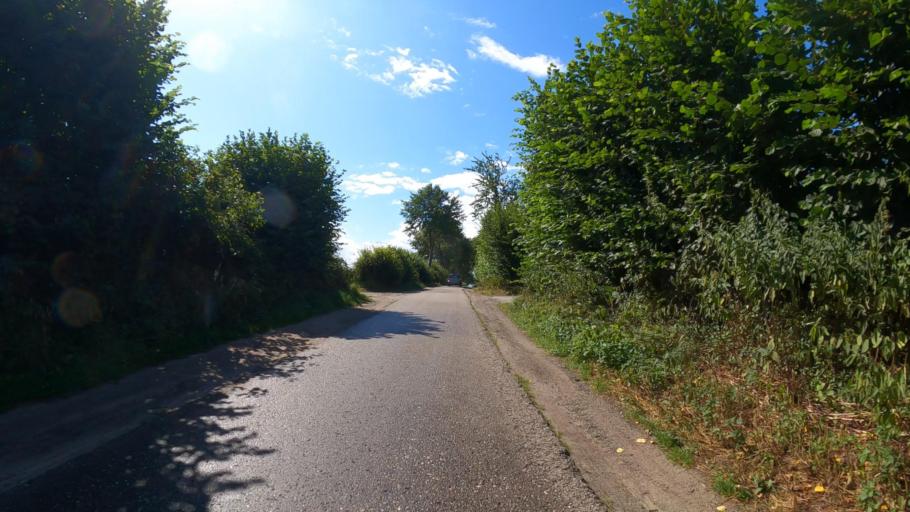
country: DE
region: Schleswig-Holstein
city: Armstedt
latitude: 53.9642
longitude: 9.8579
